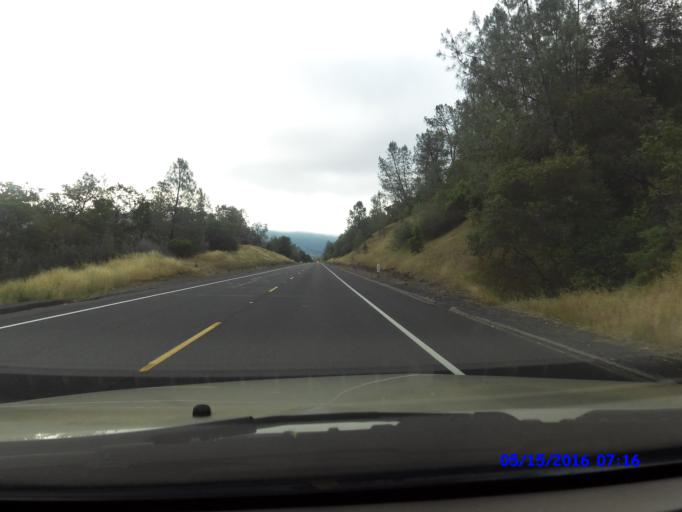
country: US
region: California
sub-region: Tuolumne County
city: East Sonora
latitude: 37.8208
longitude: -120.3269
